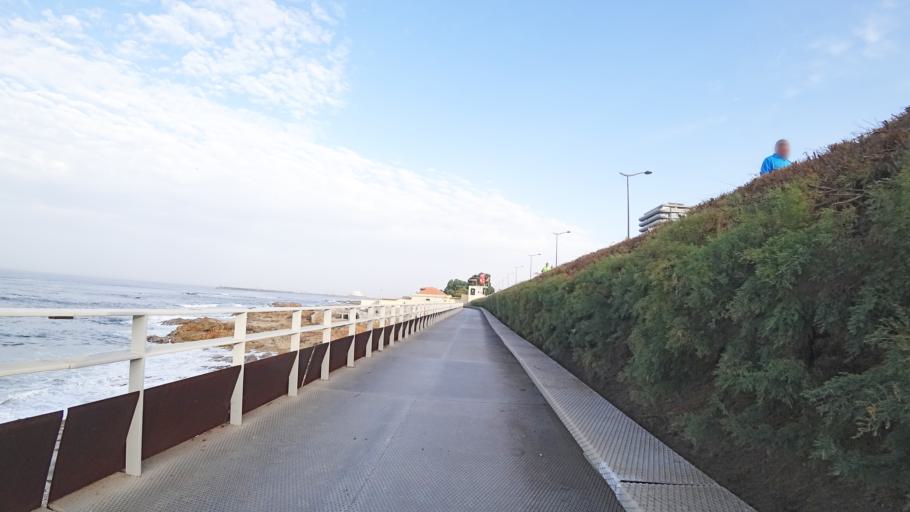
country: PT
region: Porto
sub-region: Matosinhos
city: Matosinhos
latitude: 41.1626
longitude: -8.6859
